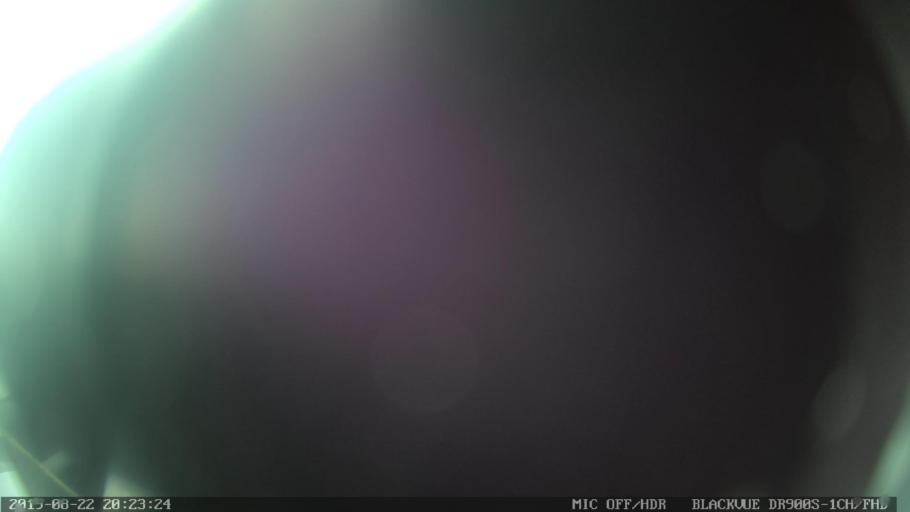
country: PT
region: Castelo Branco
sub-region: Castelo Branco
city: Castelo Branco
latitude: 39.8483
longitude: -7.5058
